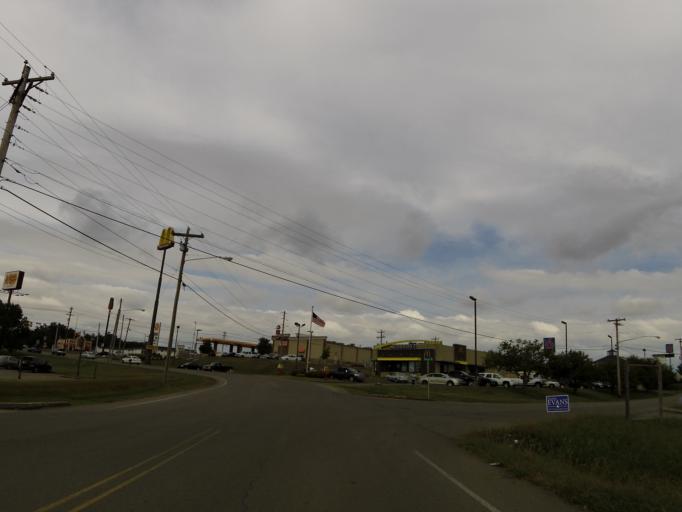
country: US
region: Tennessee
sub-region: Dickson County
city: Burns
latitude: 36.0222
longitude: -87.3371
